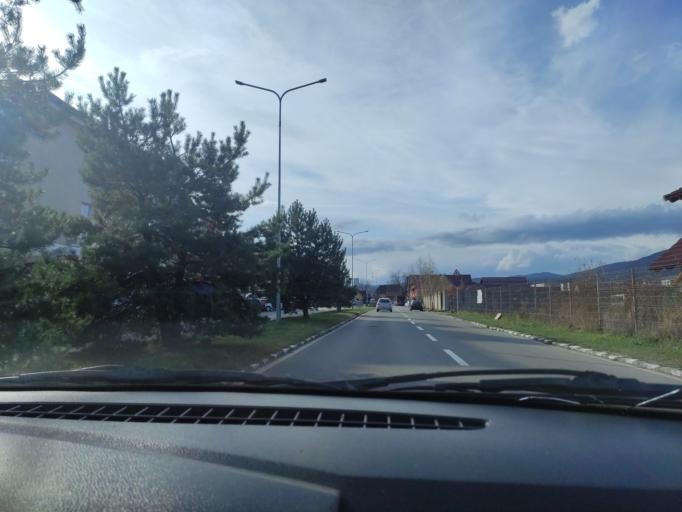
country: RO
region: Brasov
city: Codlea
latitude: 45.6928
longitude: 25.4473
